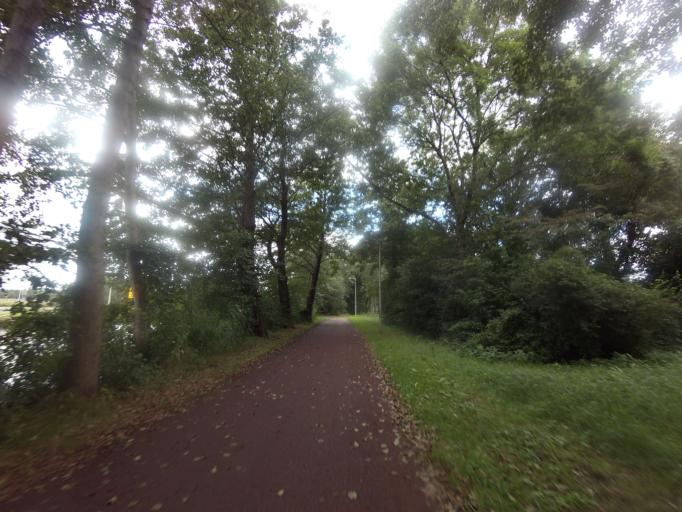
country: NL
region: Drenthe
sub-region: Gemeente Meppel
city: Meppel
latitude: 52.6924
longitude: 6.2136
